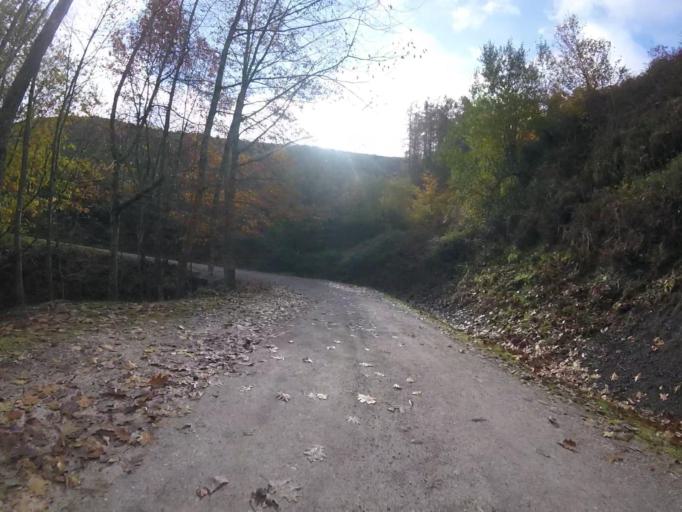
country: ES
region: Navarre
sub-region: Provincia de Navarra
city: Goizueta
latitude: 43.2073
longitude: -1.8341
